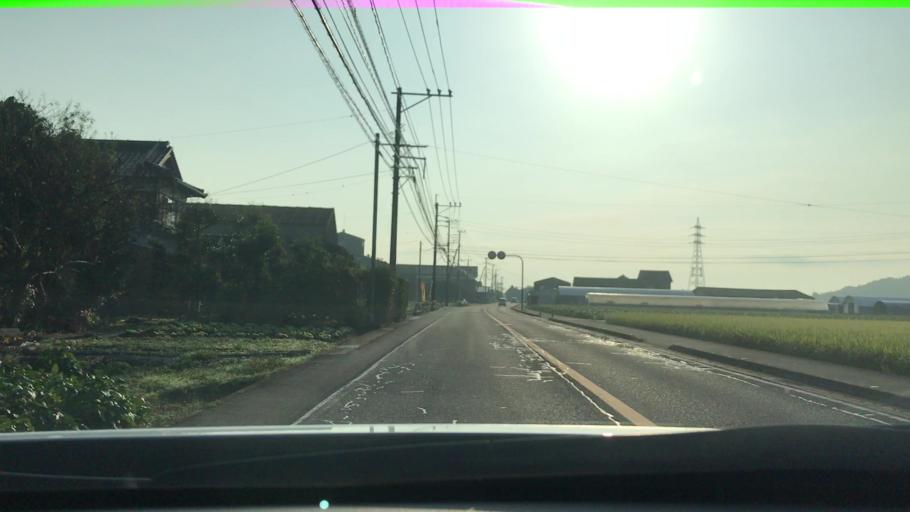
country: JP
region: Saga Prefecture
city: Takeocho-takeo
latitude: 33.2079
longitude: 130.0787
